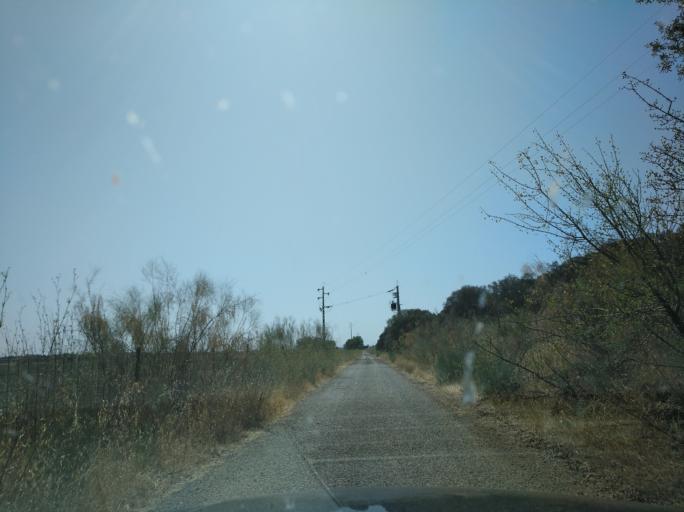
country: PT
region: Portalegre
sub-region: Campo Maior
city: Campo Maior
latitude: 39.0588
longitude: -7.0068
